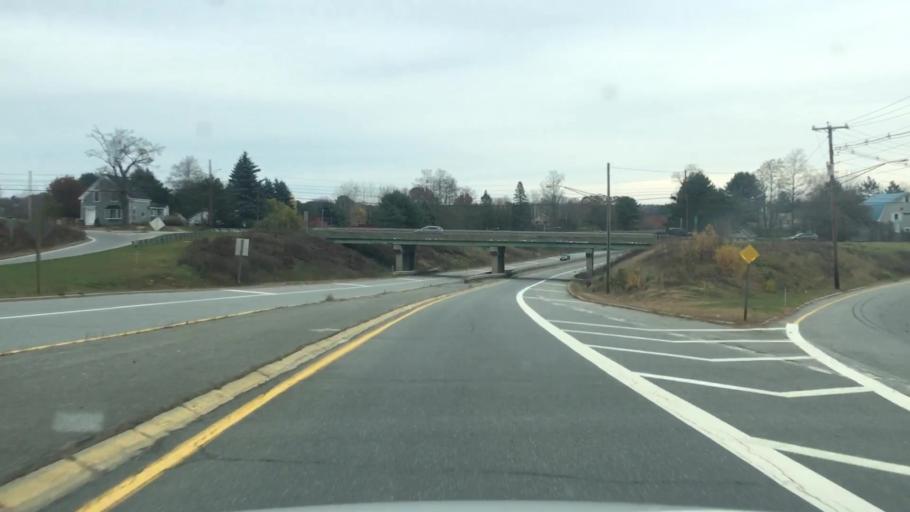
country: US
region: Maine
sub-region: Waldo County
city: Belfast
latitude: 44.4306
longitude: -69.0190
